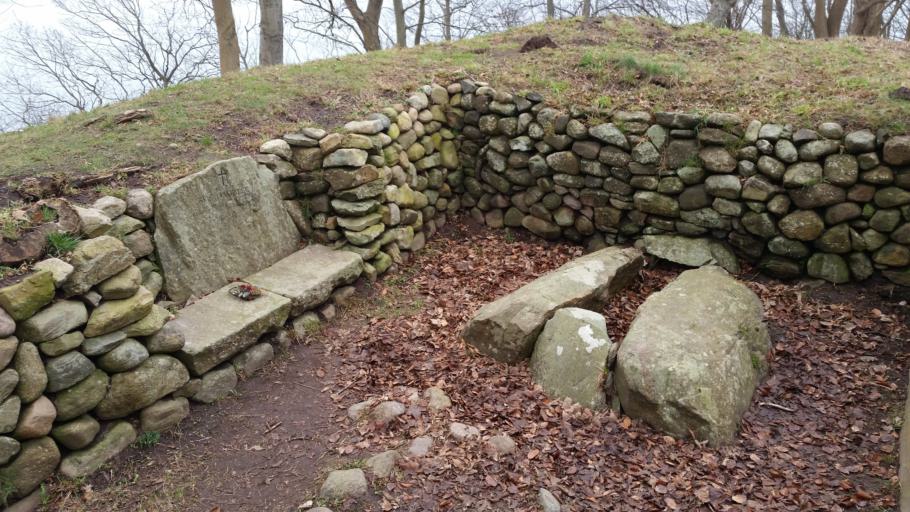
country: DK
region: Capital Region
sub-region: Gribskov Kommune
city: Gilleleje
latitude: 56.1175
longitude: 12.3538
